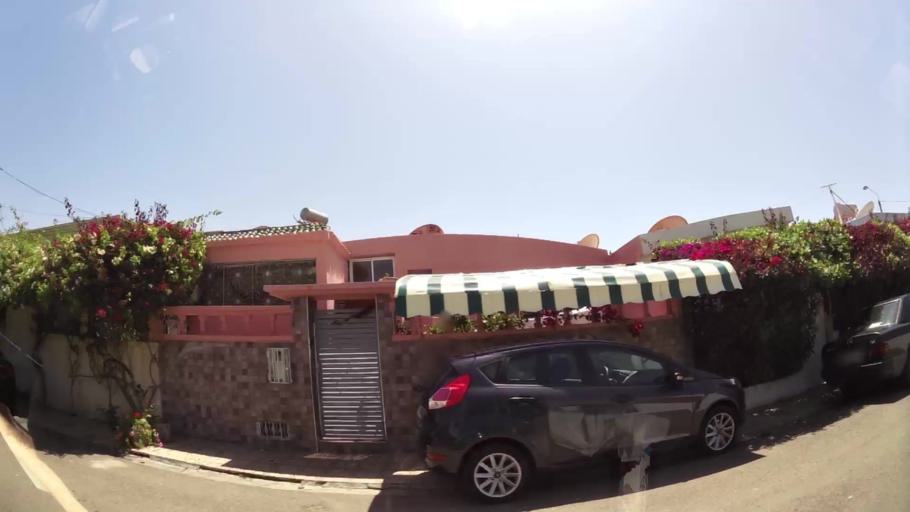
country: MA
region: Souss-Massa-Draa
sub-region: Agadir-Ida-ou-Tnan
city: Agadir
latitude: 30.4307
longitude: -9.5965
